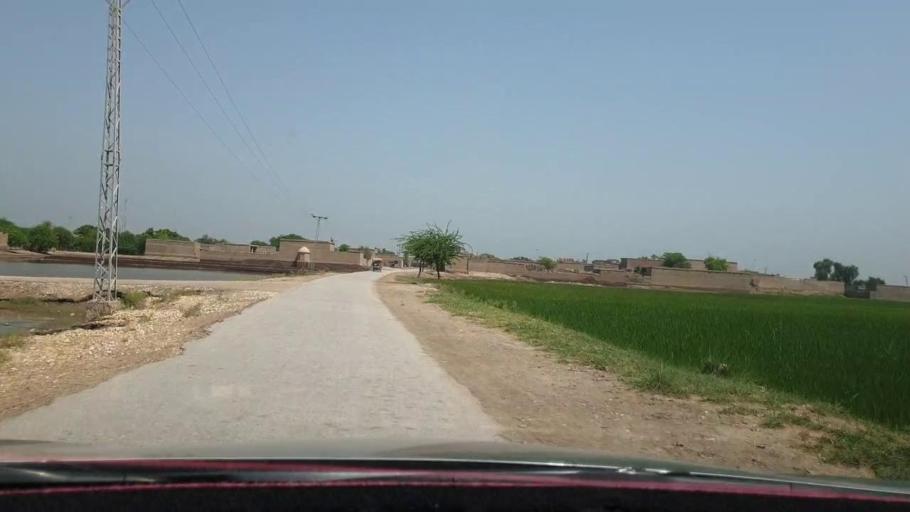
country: PK
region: Sindh
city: Warah
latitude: 27.4419
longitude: 67.7773
